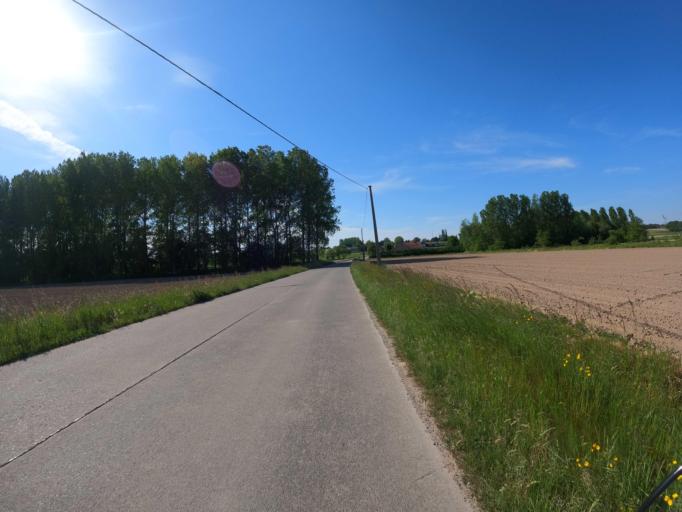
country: BE
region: Flanders
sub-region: Provincie Oost-Vlaanderen
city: Oosterzele
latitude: 50.9378
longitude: 3.7497
